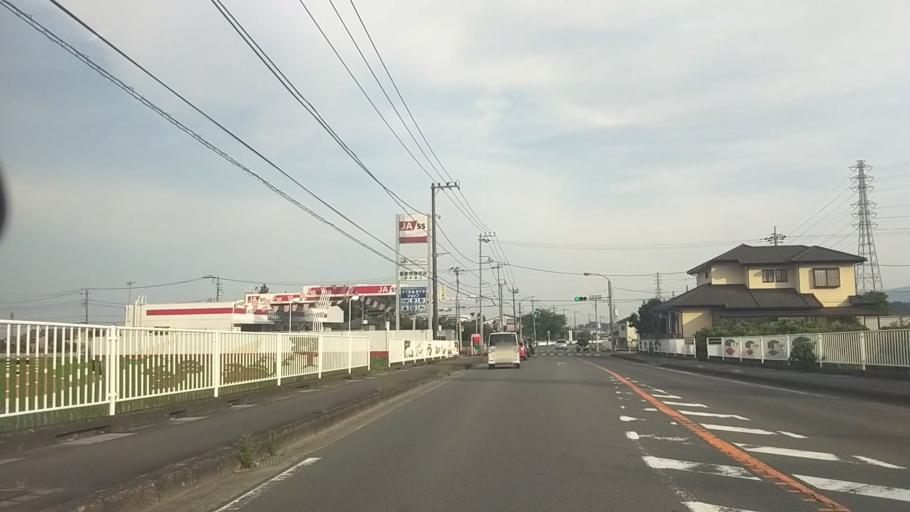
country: JP
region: Kanagawa
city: Odawara
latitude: 35.3373
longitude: 139.1050
